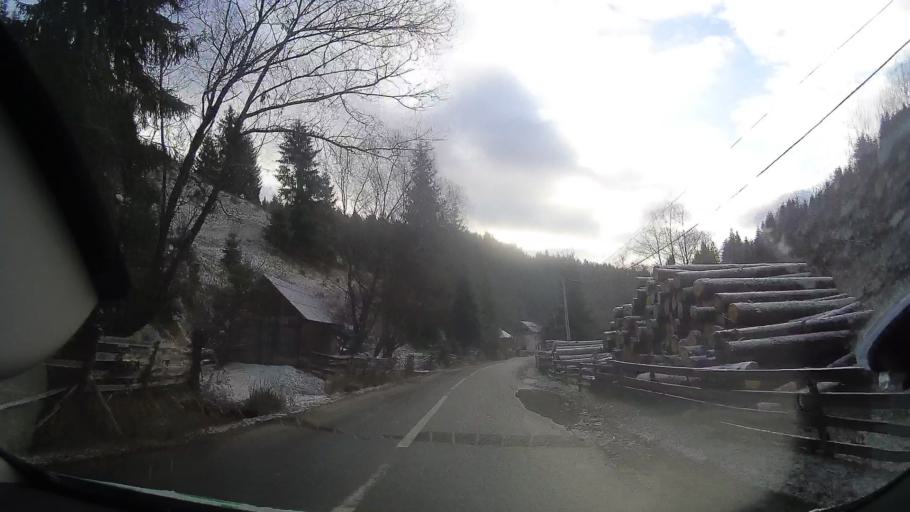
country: RO
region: Alba
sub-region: Comuna Horea
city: Horea
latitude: 46.4951
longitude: 22.9594
